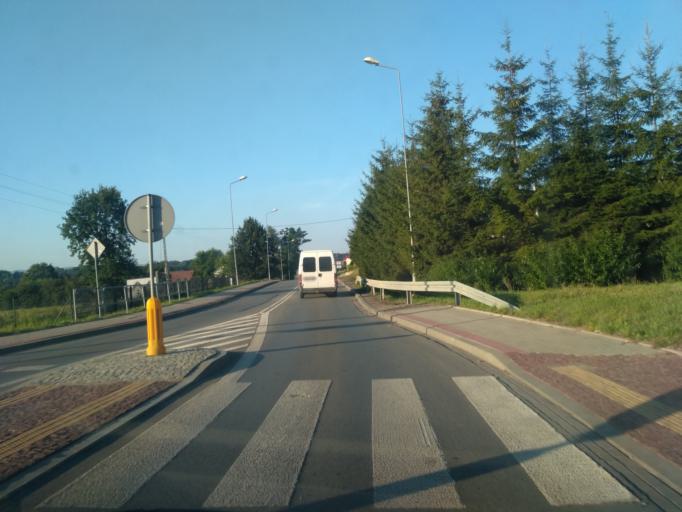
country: PL
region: Subcarpathian Voivodeship
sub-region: Krosno
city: Krosno
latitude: 49.7044
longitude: 21.7872
